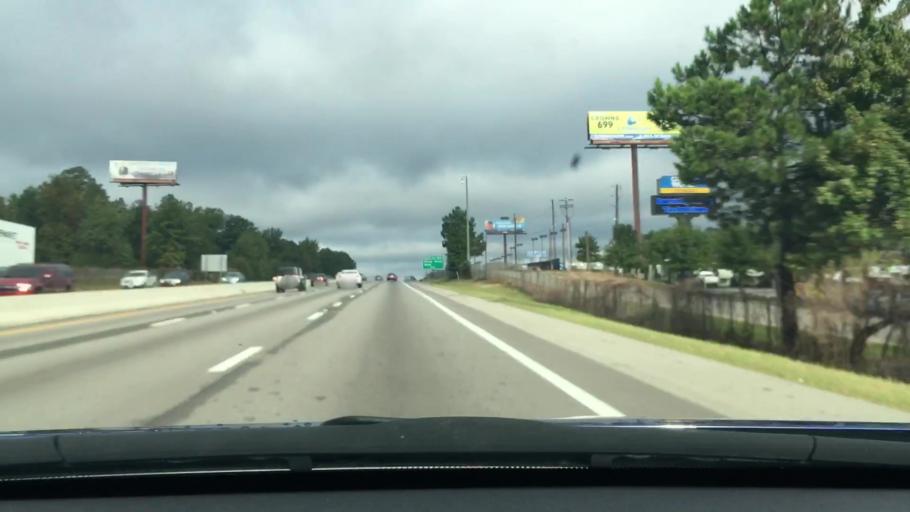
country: US
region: South Carolina
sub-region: Lexington County
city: Saint Andrews
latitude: 34.0526
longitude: -81.1263
